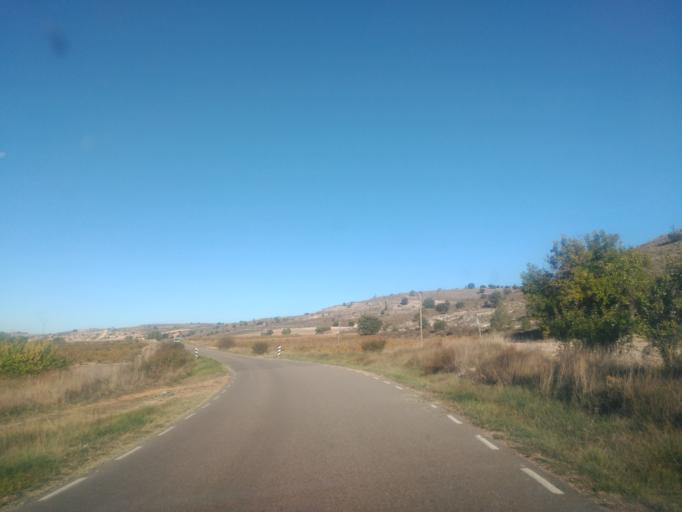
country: ES
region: Castille and Leon
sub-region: Provincia de Burgos
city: Penaranda de Duero
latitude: 41.6854
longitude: -3.4354
